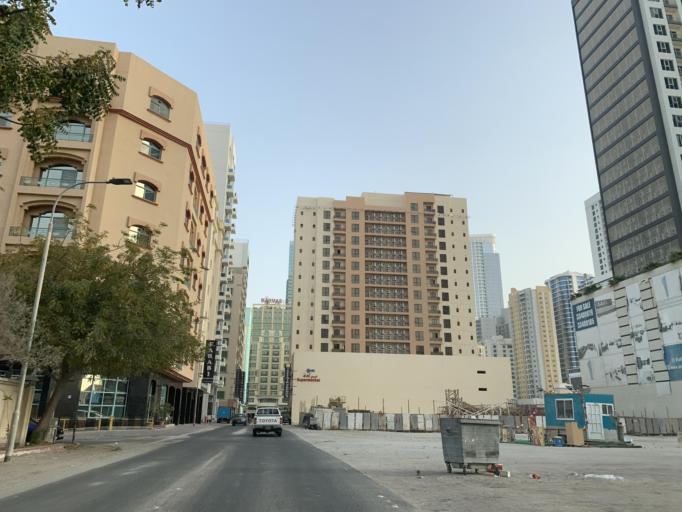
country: BH
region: Manama
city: Manama
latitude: 26.2186
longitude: 50.6088
